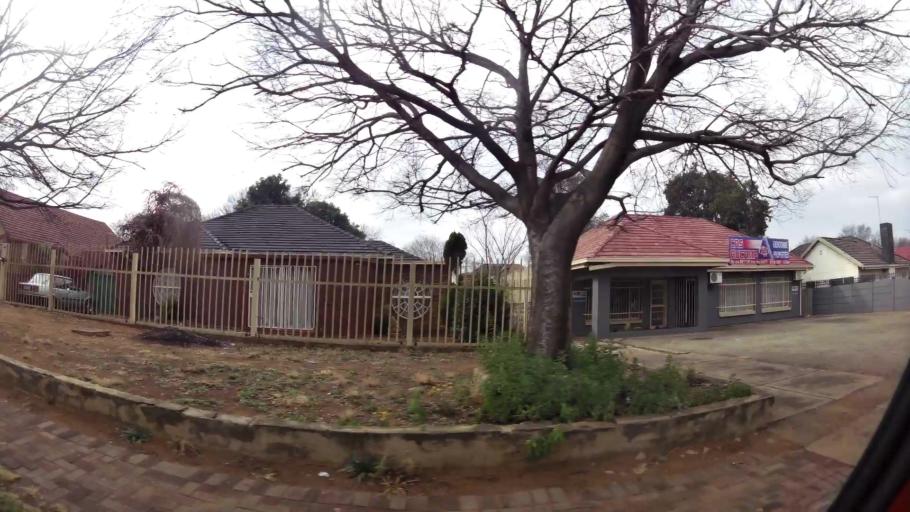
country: ZA
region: Gauteng
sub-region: Sedibeng District Municipality
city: Vanderbijlpark
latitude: -26.6989
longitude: 27.8406
